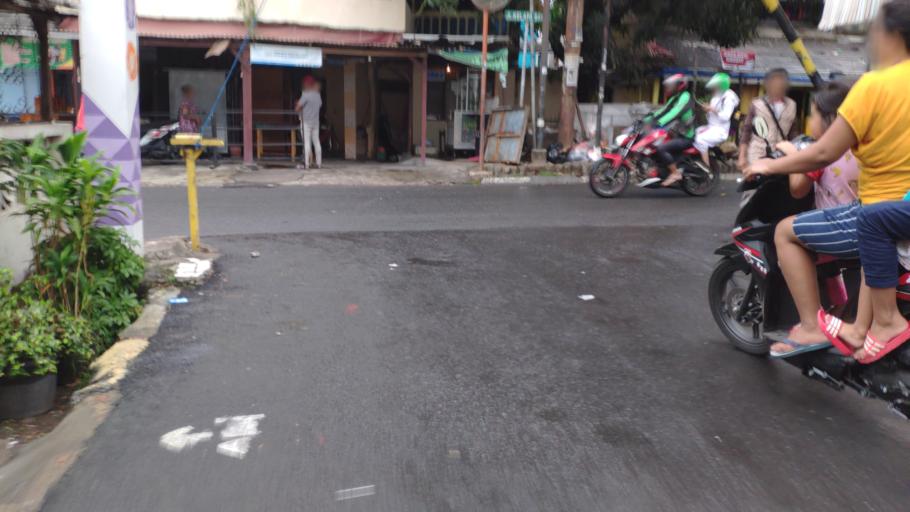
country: ID
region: Jakarta Raya
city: Jakarta
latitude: -6.2075
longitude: 106.8659
